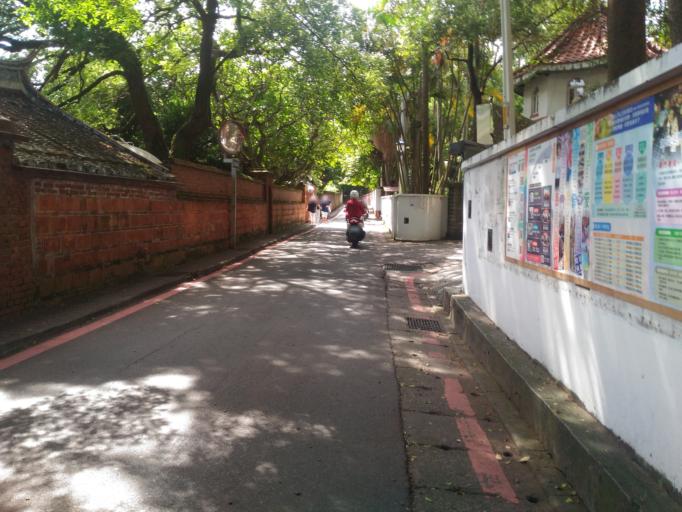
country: TW
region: Taipei
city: Taipei
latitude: 25.1748
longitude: 121.4361
